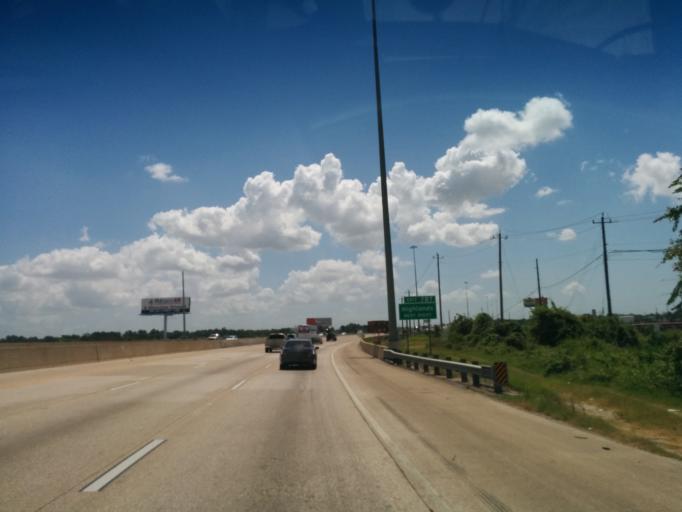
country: US
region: Texas
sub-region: Harris County
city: Highlands
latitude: 29.7952
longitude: -95.0688
